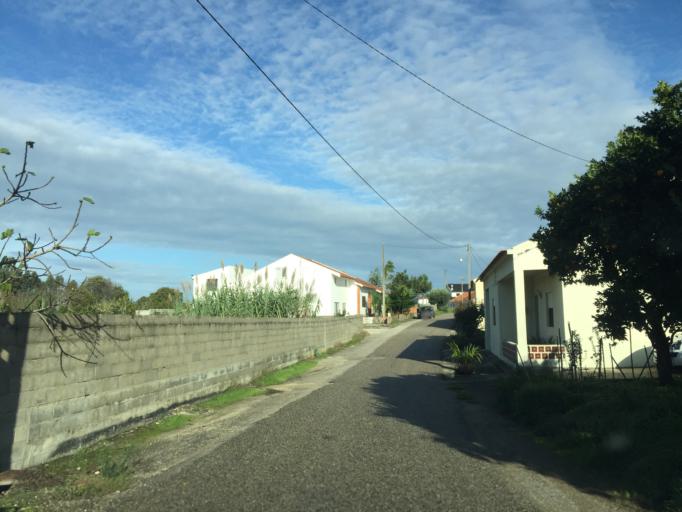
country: PT
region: Coimbra
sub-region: Figueira da Foz
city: Lavos
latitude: 40.0516
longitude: -8.7914
